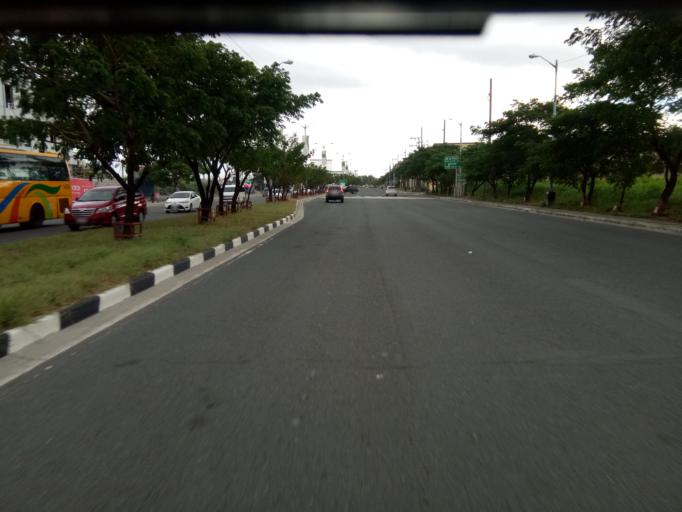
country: PH
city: Sambayanihan People's Village
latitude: 14.5121
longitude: 120.9898
